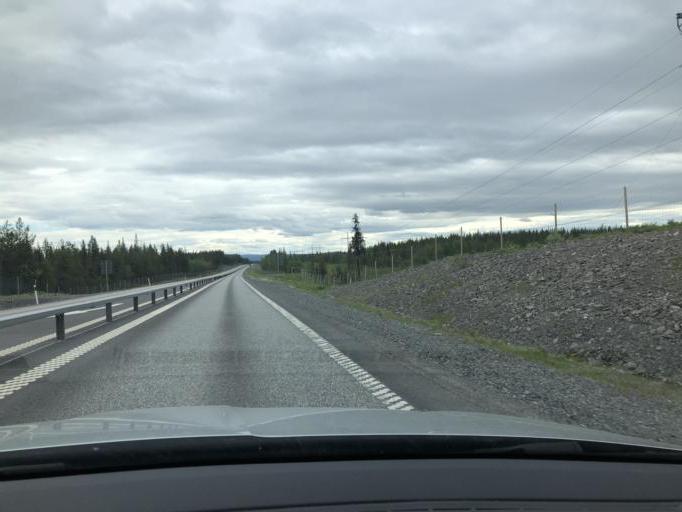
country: SE
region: Norrbotten
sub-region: Gallivare Kommun
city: Malmberget
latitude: 67.6871
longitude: 20.8509
